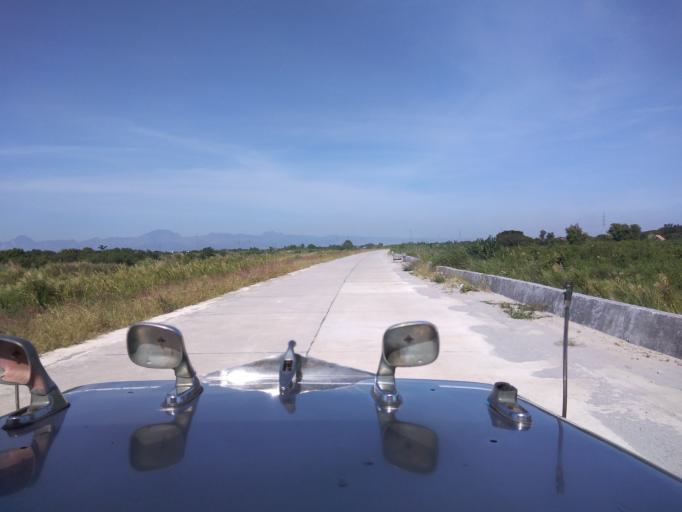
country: PH
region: Central Luzon
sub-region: Province of Pampanga
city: Bacolor
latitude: 14.9961
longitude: 120.6665
